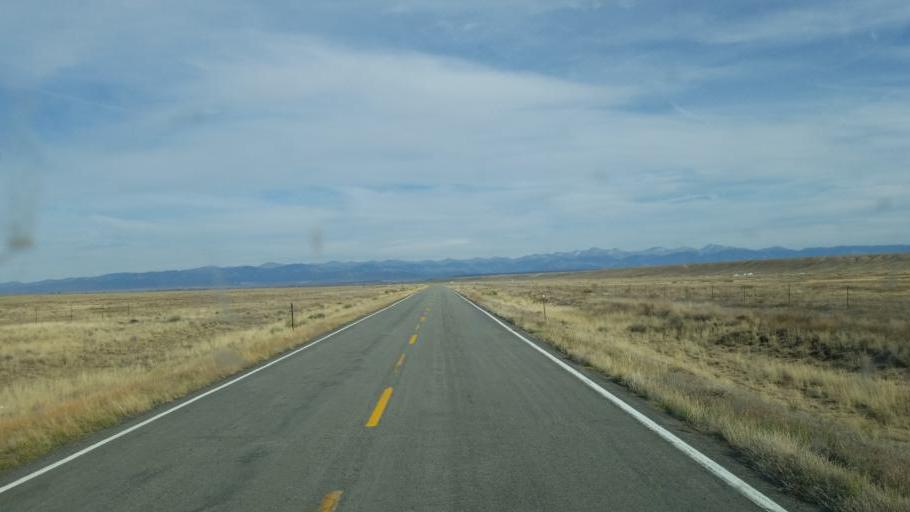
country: US
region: Colorado
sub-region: Costilla County
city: San Luis
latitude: 37.1806
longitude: -105.6273
